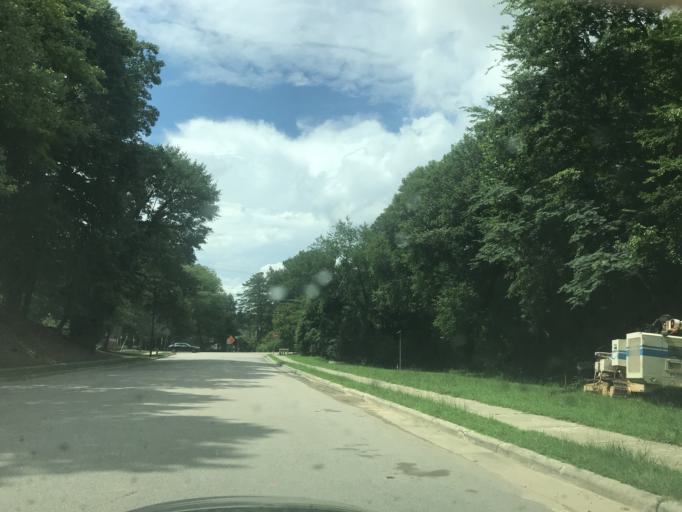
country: US
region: North Carolina
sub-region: Wake County
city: West Raleigh
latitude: 35.8202
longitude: -78.6337
